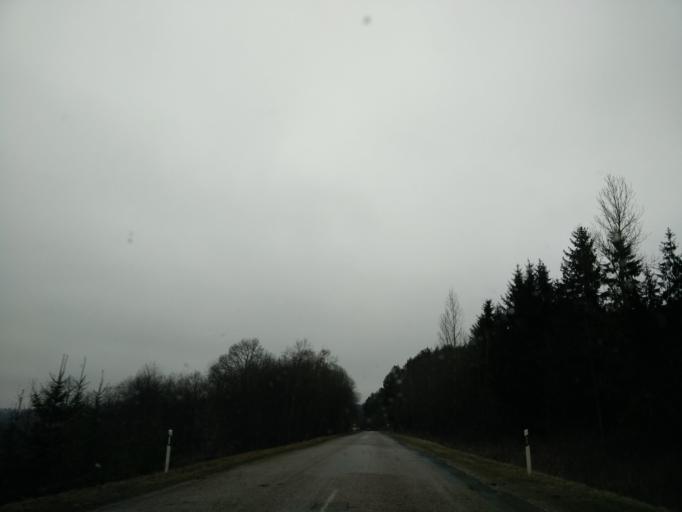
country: LT
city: Ariogala
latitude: 55.2936
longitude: 23.4424
